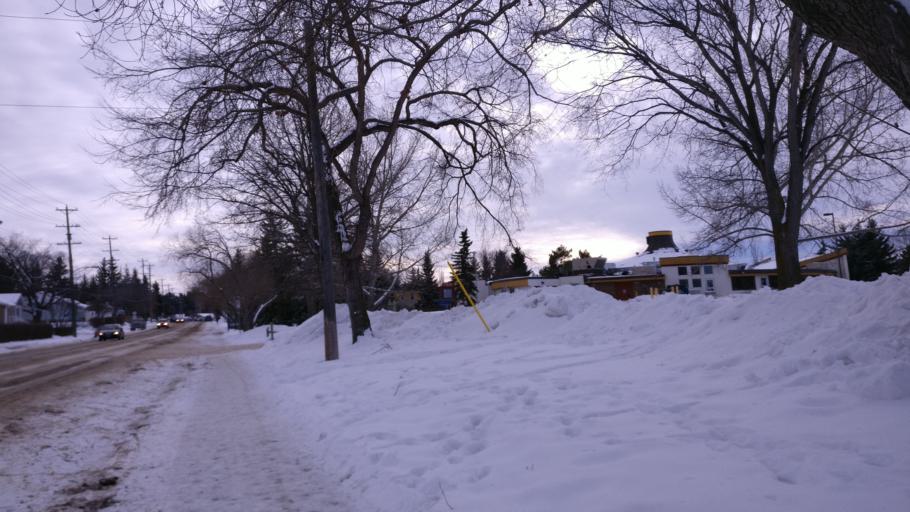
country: CA
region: Alberta
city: Red Deer
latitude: 52.2662
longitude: -113.8051
